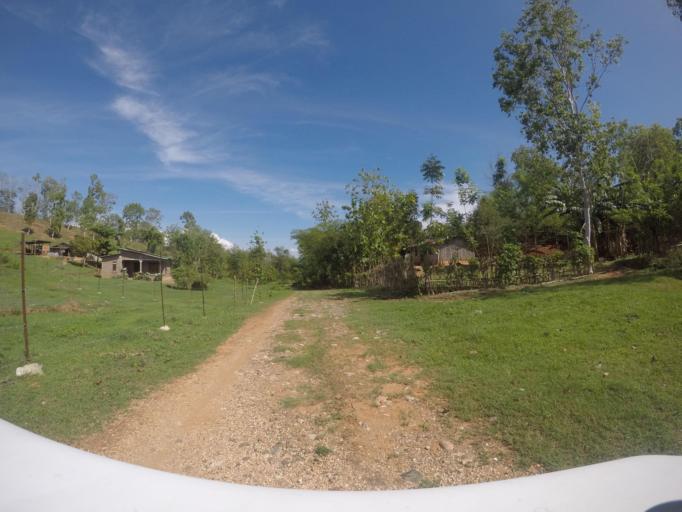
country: TL
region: Bobonaro
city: Maliana
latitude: -8.9820
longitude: 125.1953
